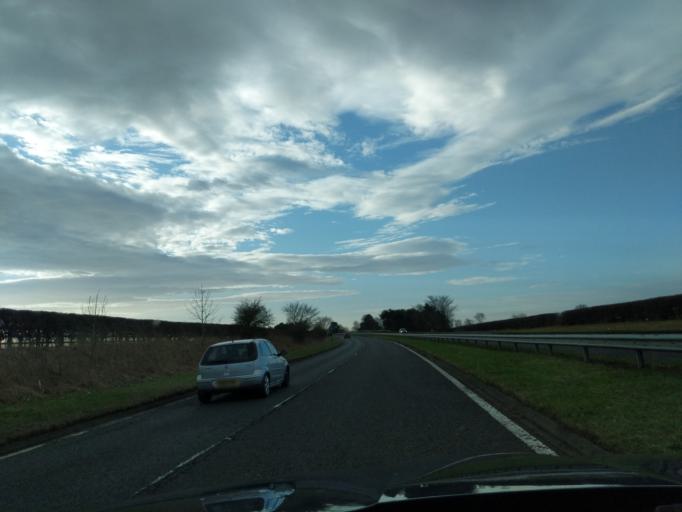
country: GB
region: England
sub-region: Northumberland
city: Cramlington
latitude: 55.0476
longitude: -1.5875
